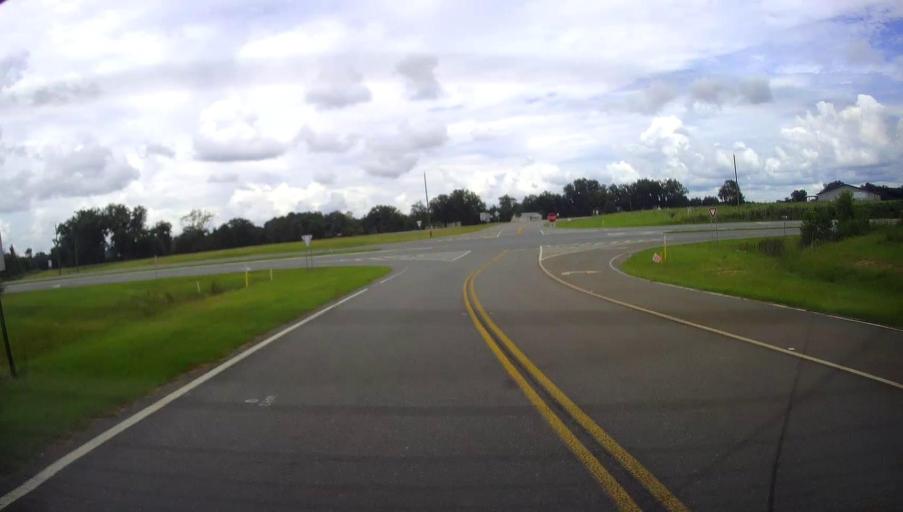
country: US
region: Georgia
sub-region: Schley County
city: Ellaville
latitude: 32.2230
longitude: -84.2866
